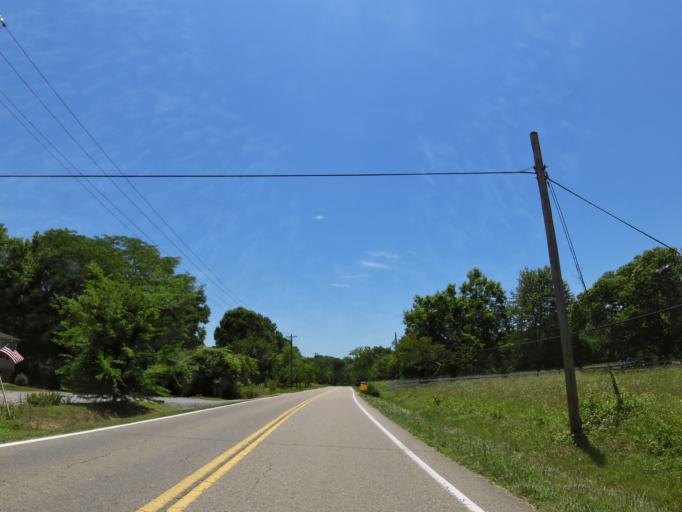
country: US
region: Tennessee
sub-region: Jefferson County
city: Dandridge
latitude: 35.9912
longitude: -83.3911
